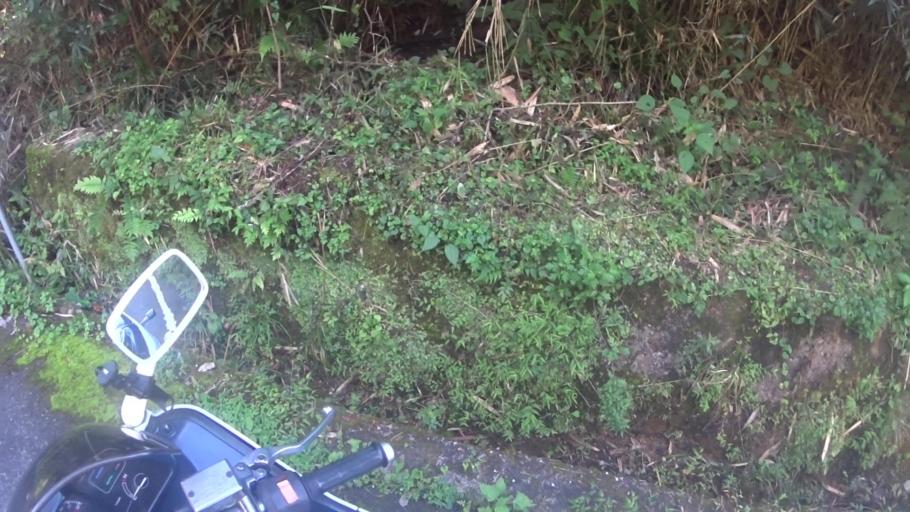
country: JP
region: Nara
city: Nara-shi
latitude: 34.7442
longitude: 135.9482
